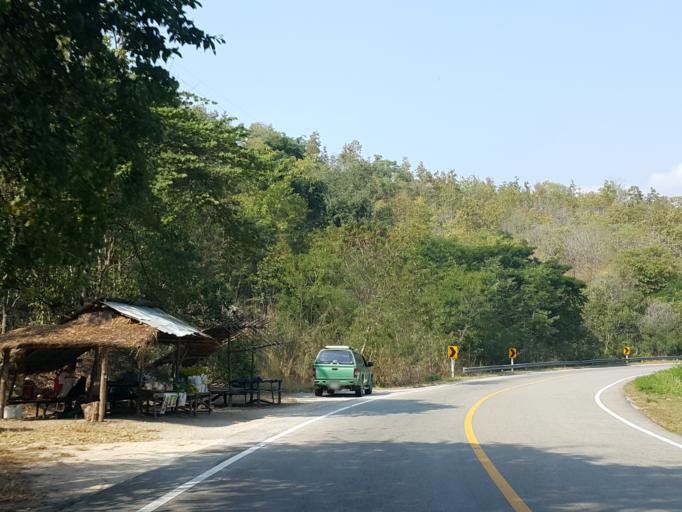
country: TH
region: Chiang Mai
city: Hot
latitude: 18.2250
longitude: 98.5676
